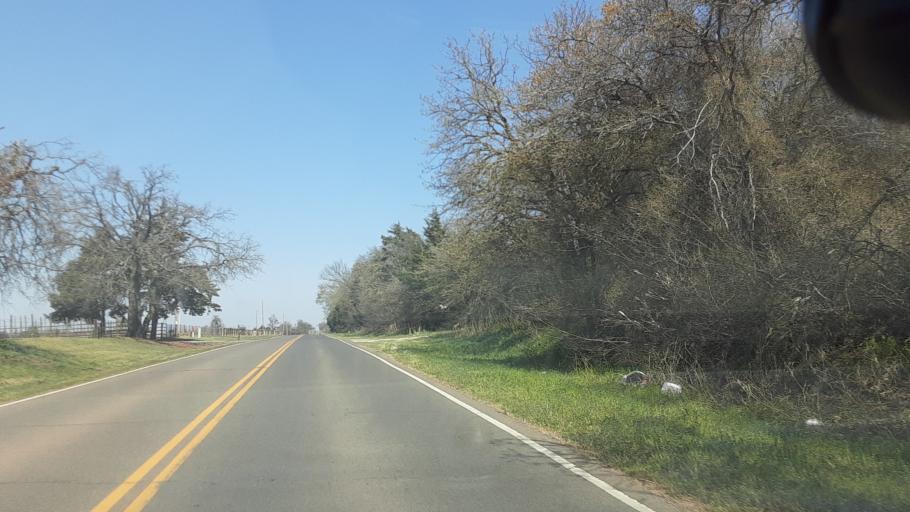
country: US
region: Oklahoma
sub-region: Logan County
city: Guthrie
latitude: 35.7733
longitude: -97.4784
